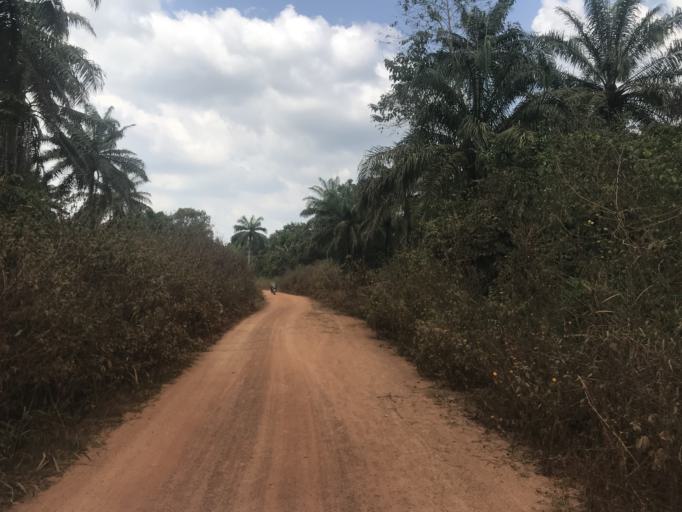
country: NG
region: Osun
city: Inisa
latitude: 7.8678
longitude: 4.3829
